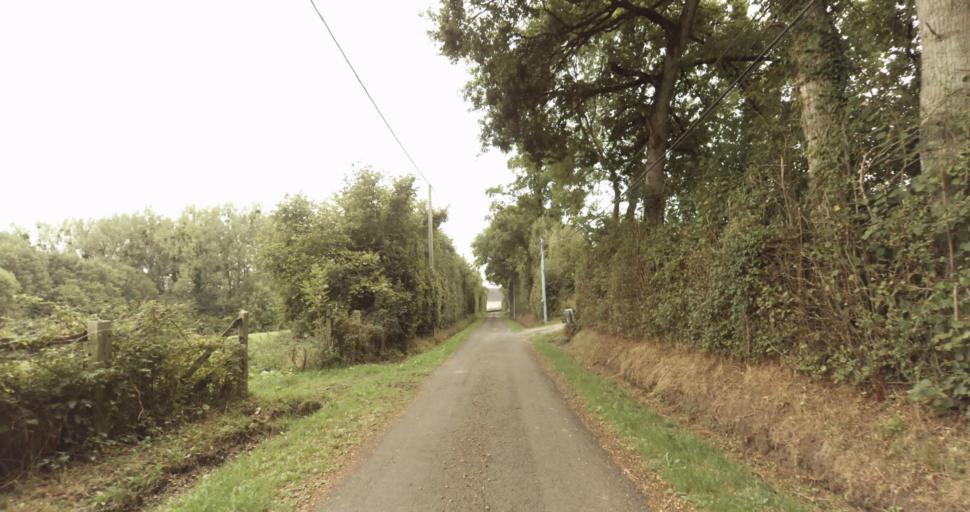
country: FR
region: Lower Normandy
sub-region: Departement de l'Orne
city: Sees
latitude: 48.6819
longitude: 0.2527
